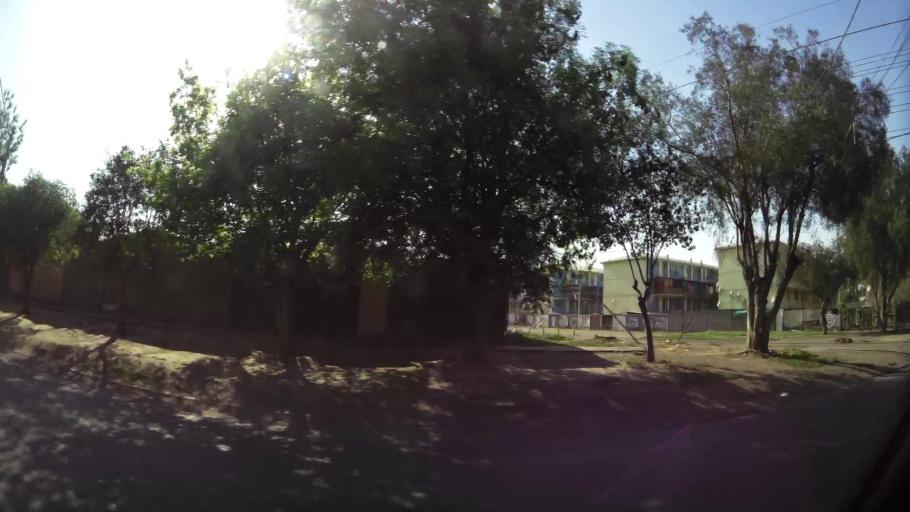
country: CL
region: Santiago Metropolitan
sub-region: Provincia de Santiago
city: Lo Prado
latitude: -33.4233
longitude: -70.7475
